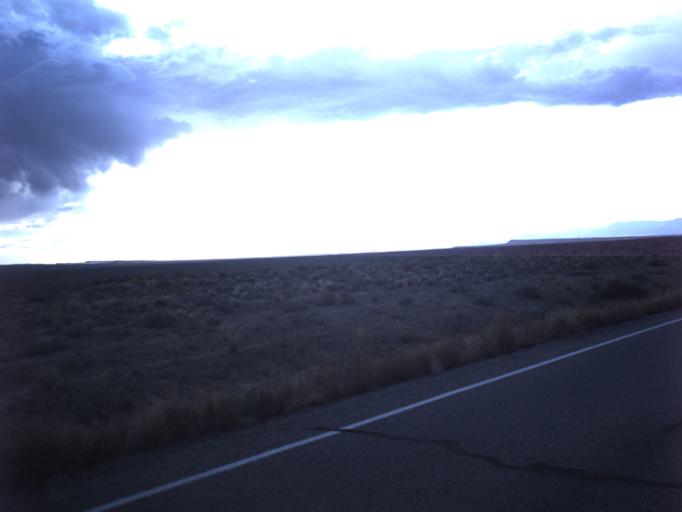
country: US
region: Utah
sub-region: Grand County
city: Moab
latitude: 38.9170
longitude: -109.3308
